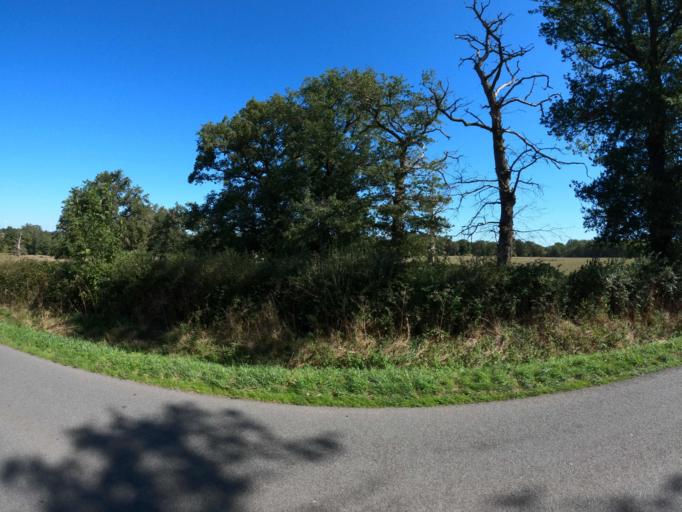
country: FR
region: Limousin
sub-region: Departement de la Haute-Vienne
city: Le Dorat
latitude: 46.2520
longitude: 1.0446
